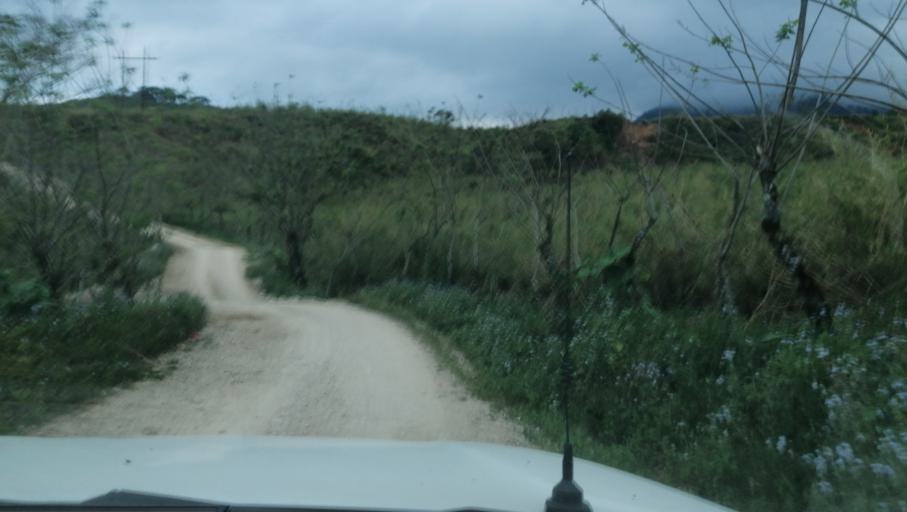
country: MX
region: Chiapas
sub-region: Francisco Leon
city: San Miguel la Sardina
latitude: 17.2906
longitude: -93.2708
